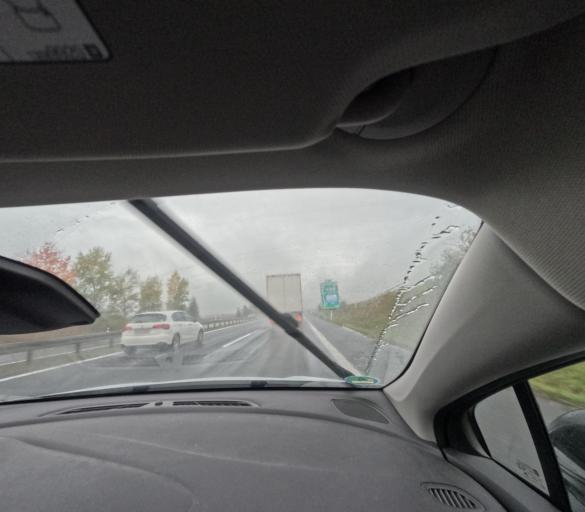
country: CZ
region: Central Bohemia
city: Velka Dobra
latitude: 50.1049
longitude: 14.0915
